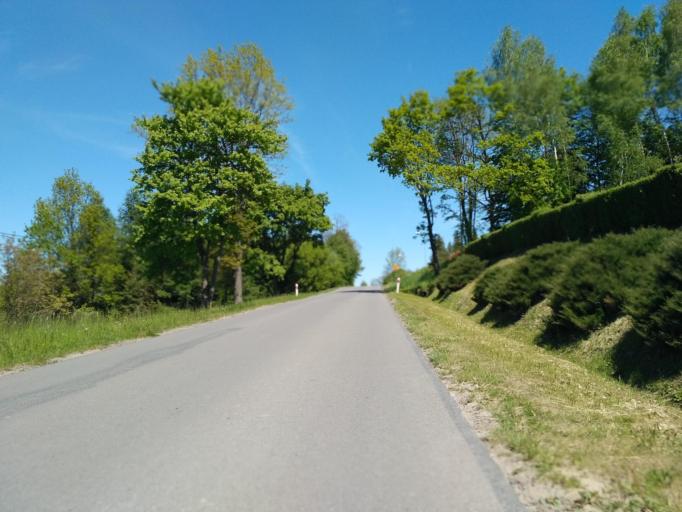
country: PL
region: Subcarpathian Voivodeship
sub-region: Powiat sanocki
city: Nowosielce-Gniewosz
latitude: 49.5321
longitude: 22.0504
